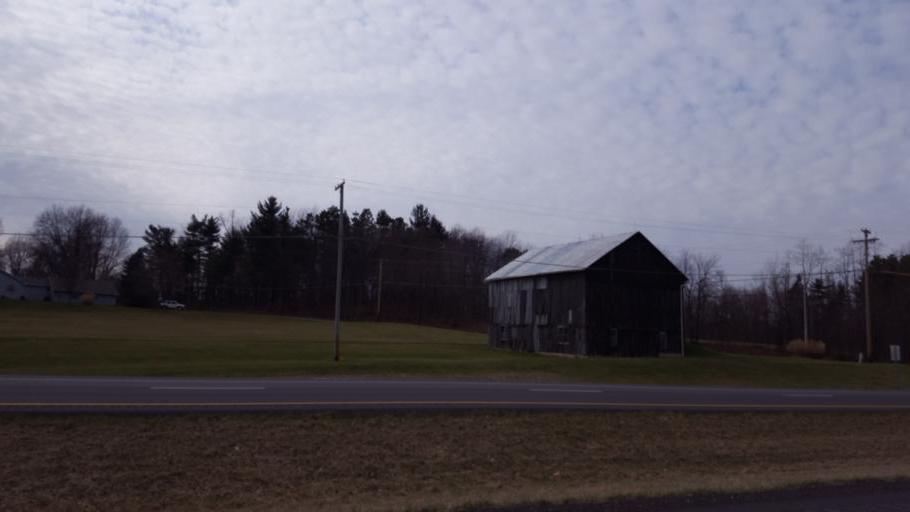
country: US
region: Ohio
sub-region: Sandusky County
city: Bellville
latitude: 40.6746
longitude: -82.5210
